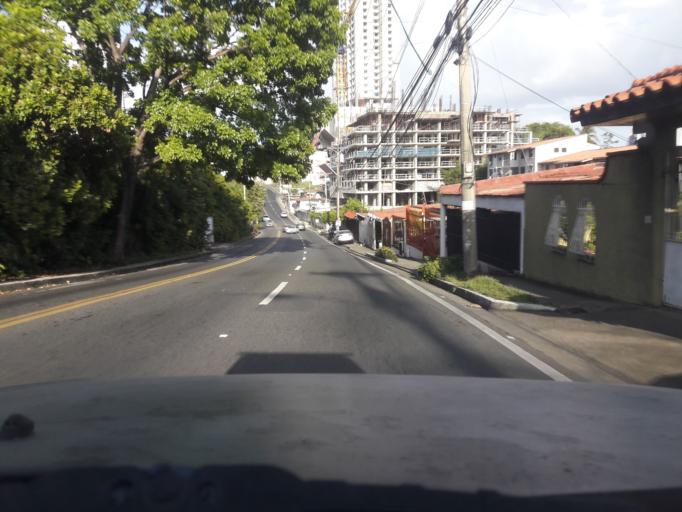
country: PA
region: Panama
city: Panama
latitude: 9.0133
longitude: -79.5092
